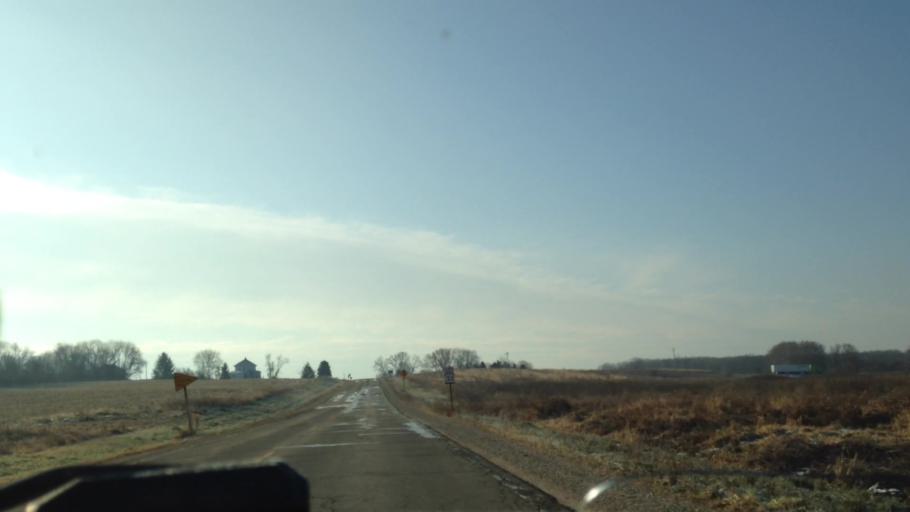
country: US
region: Wisconsin
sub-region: Dodge County
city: Mayville
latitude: 43.4467
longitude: -88.5001
